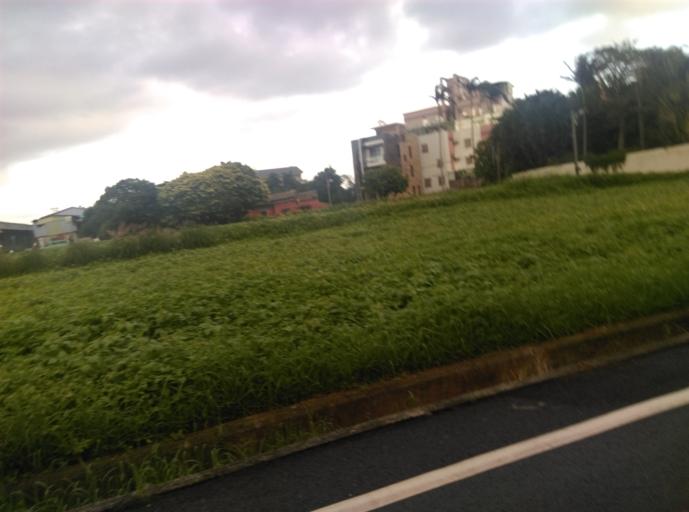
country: TW
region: Taiwan
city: Taoyuan City
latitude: 24.9928
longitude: 121.2527
